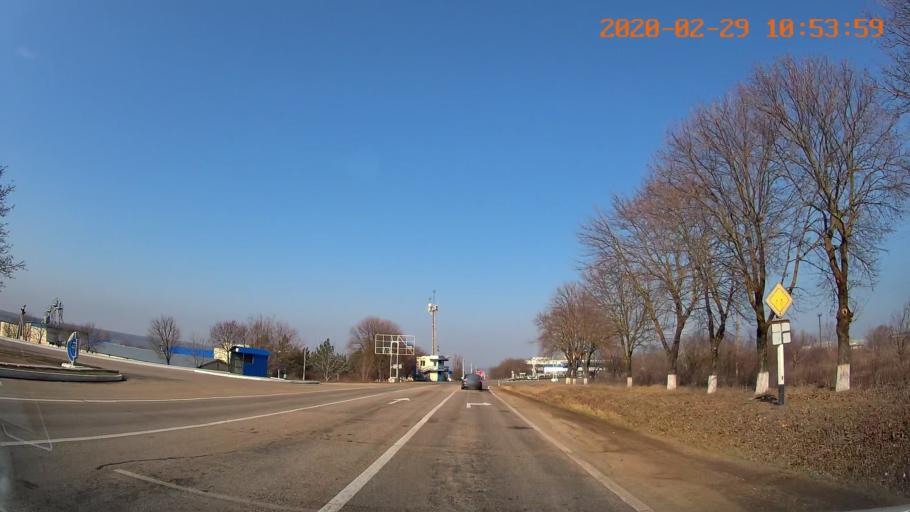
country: MD
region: Telenesti
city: Grigoriopol
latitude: 47.1194
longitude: 29.3292
